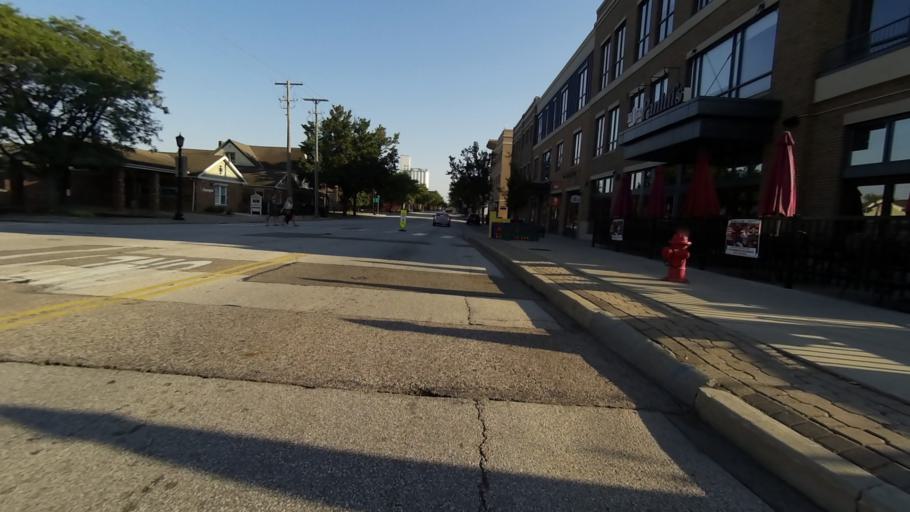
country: US
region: Ohio
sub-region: Portage County
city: Kent
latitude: 41.1515
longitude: -81.3581
